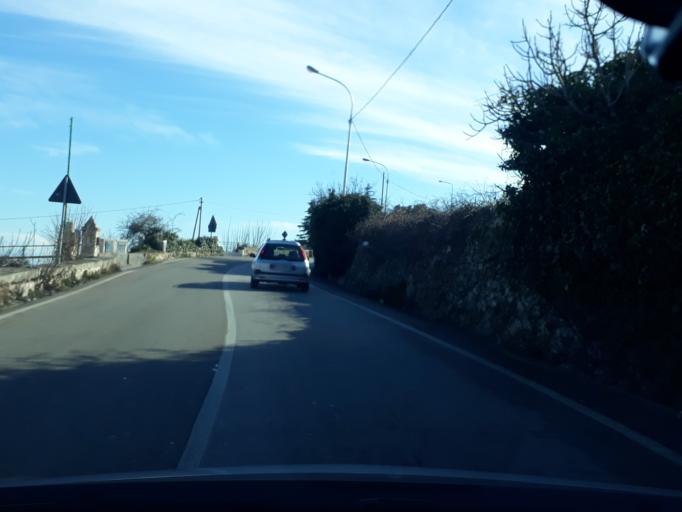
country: IT
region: Apulia
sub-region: Provincia di Taranto
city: Martina Franca
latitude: 40.7092
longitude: 17.3366
